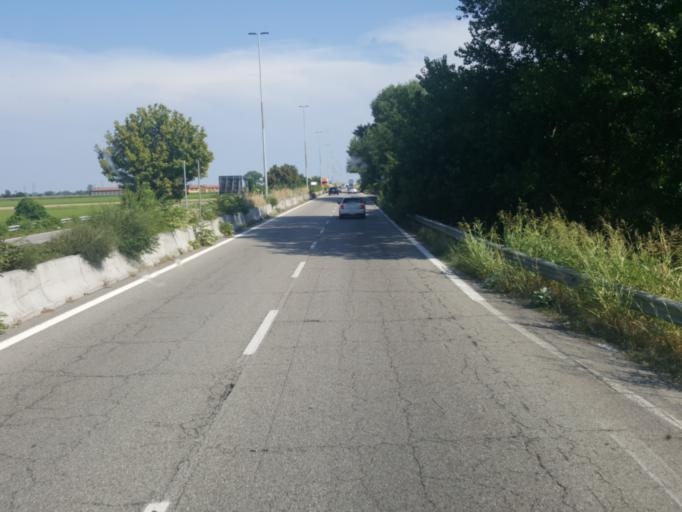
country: IT
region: Lombardy
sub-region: Citta metropolitana di Milano
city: Opera
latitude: 45.3835
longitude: 9.2170
